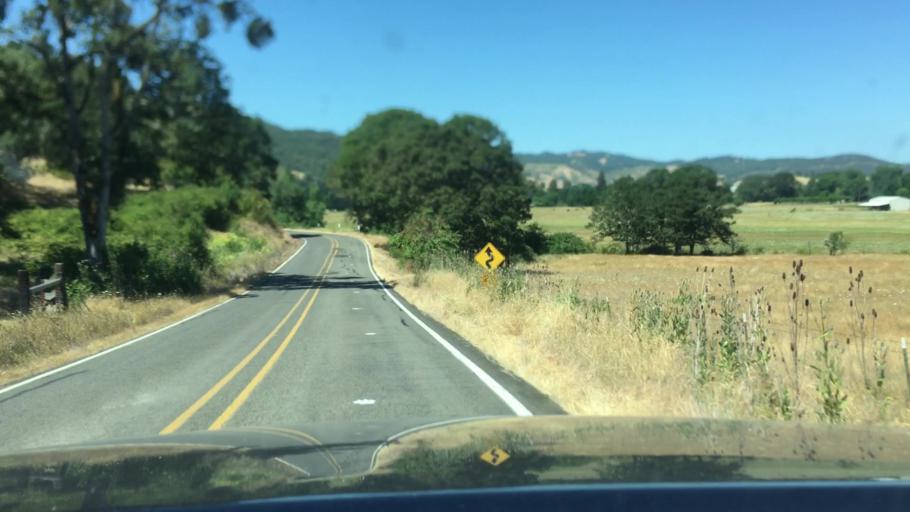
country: US
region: Oregon
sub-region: Douglas County
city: Winston
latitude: 43.1337
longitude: -123.4121
